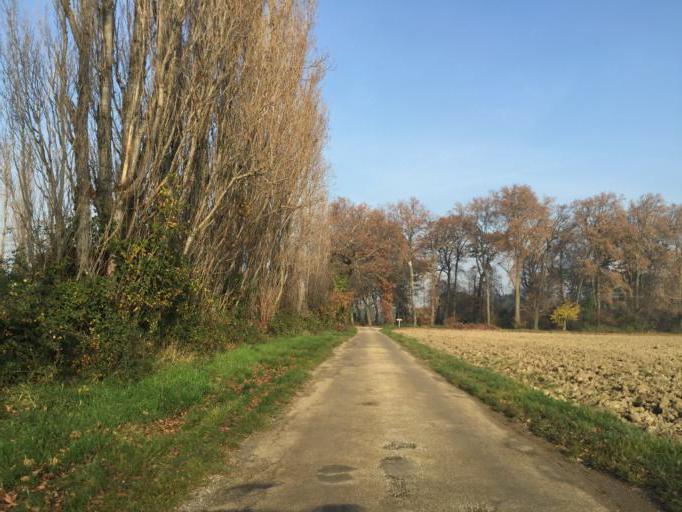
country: FR
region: Provence-Alpes-Cote d'Azur
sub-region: Departement du Vaucluse
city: Jonquieres
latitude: 44.1051
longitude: 4.9096
